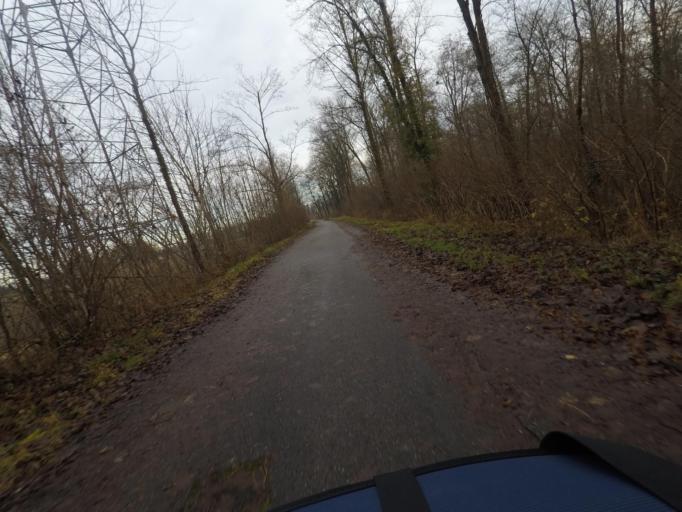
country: DE
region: Baden-Wuerttemberg
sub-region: Karlsruhe Region
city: Rheinau
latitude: 48.8717
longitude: 8.1739
